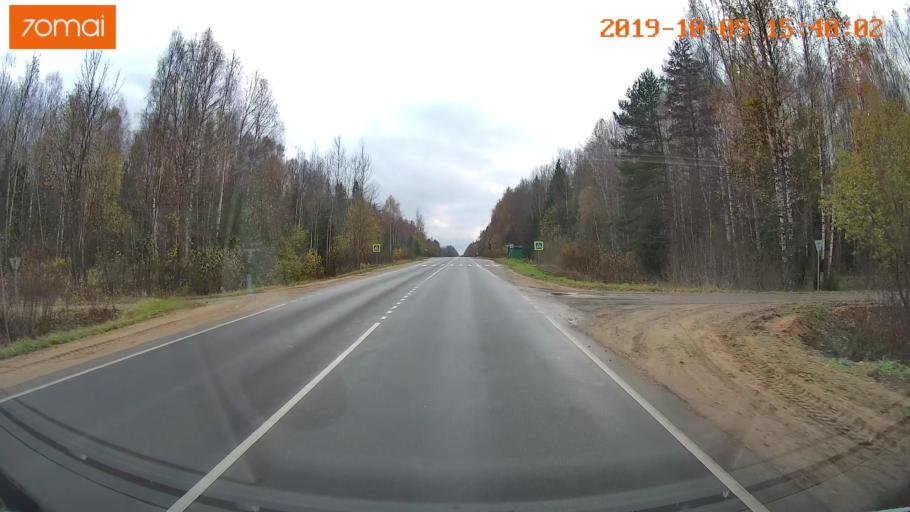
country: RU
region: Kostroma
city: Oktyabr'skiy
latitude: 57.8915
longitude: 41.1526
